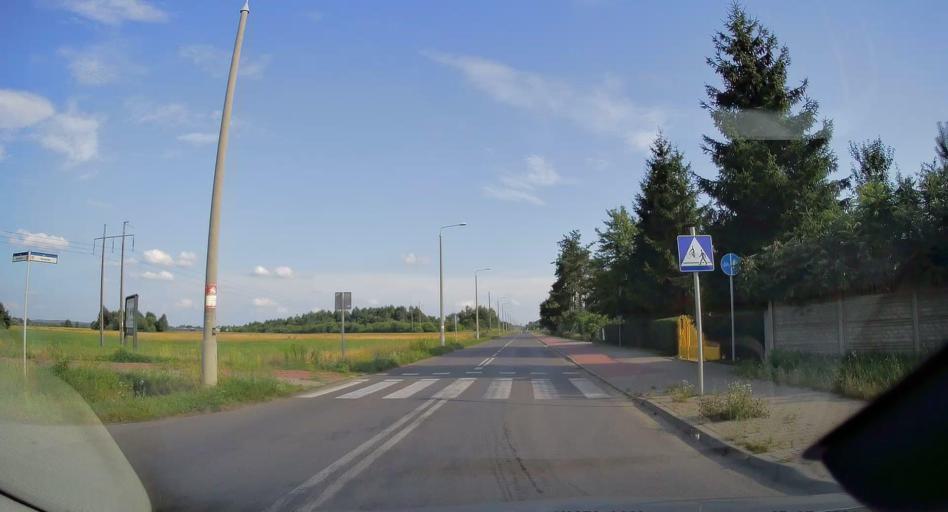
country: PL
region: Swietokrzyskie
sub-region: Powiat konecki
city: Konskie
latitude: 51.2175
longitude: 20.3906
